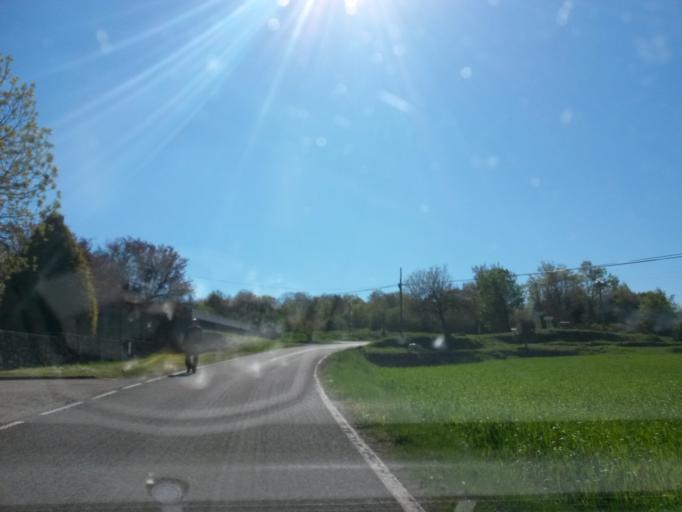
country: ES
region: Catalonia
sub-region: Provincia de Girona
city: Sant Cristofol de les Fonts
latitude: 42.1727
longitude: 2.5185
